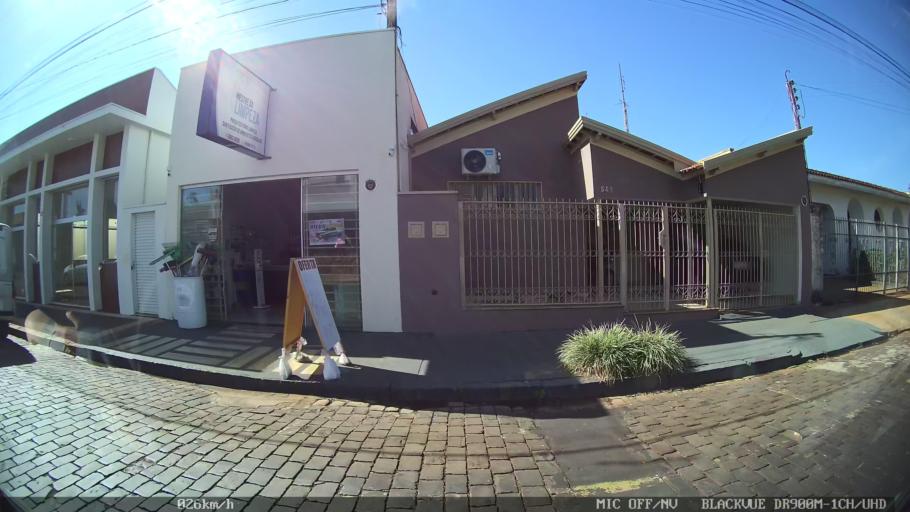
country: BR
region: Sao Paulo
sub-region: Batatais
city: Batatais
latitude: -20.8938
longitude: -47.5834
